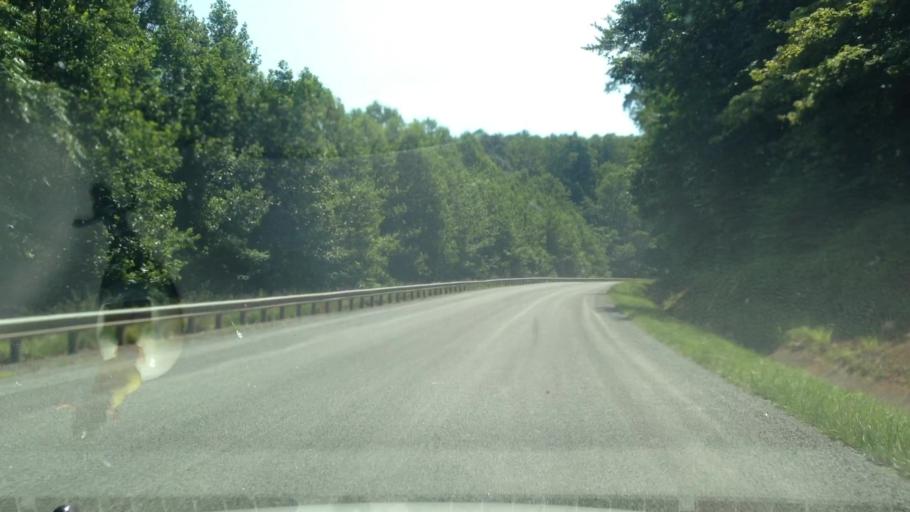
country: US
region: Virginia
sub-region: Patrick County
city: Stuart
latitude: 36.5991
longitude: -80.3007
